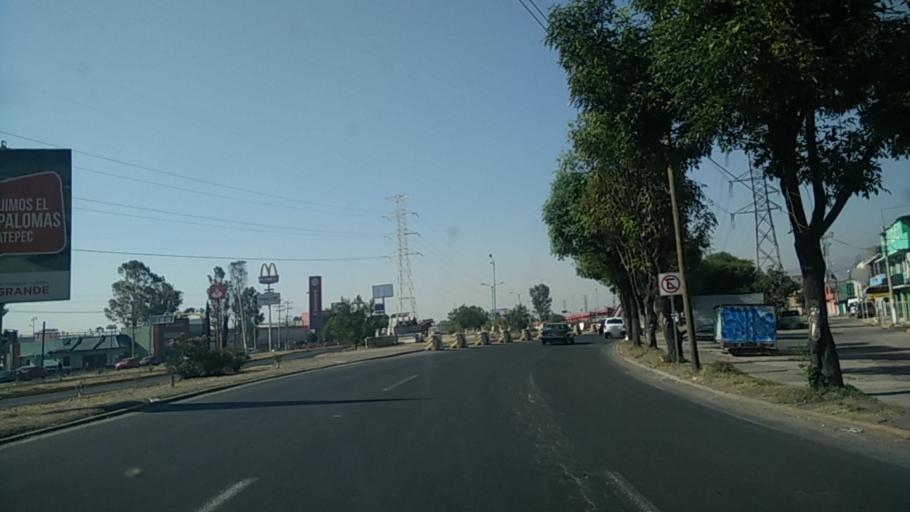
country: MX
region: Mexico
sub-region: Atenco
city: Colonia el Salado
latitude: 19.6063
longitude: -99.0124
